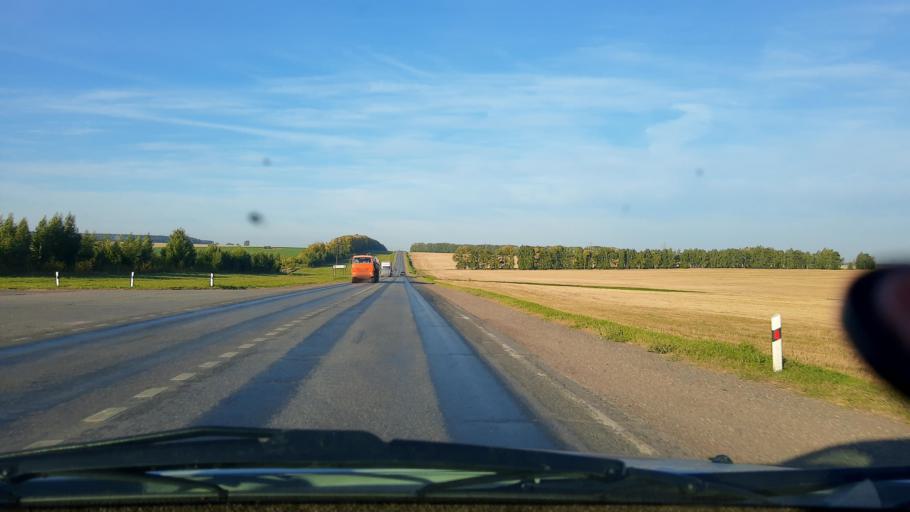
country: RU
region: Bashkortostan
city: Ulukulevo
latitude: 54.4037
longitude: 56.2924
